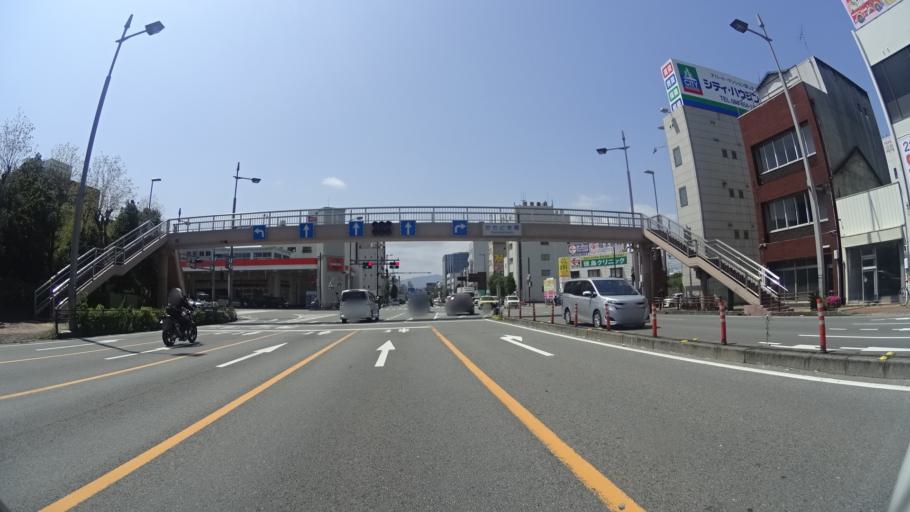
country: JP
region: Tokushima
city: Tokushima-shi
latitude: 34.0661
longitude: 134.5571
